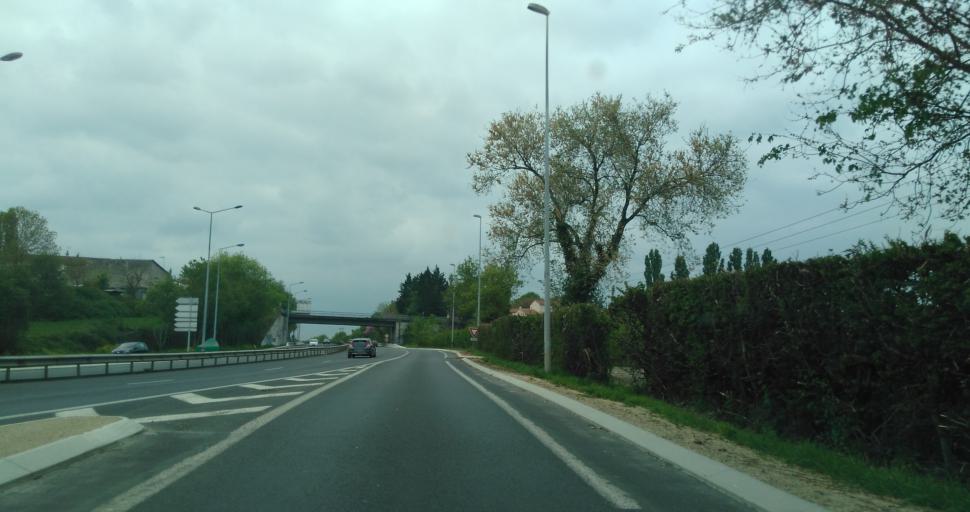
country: FR
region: Poitou-Charentes
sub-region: Departement des Deux-Sevres
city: Niort
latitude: 46.3366
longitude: -0.4536
